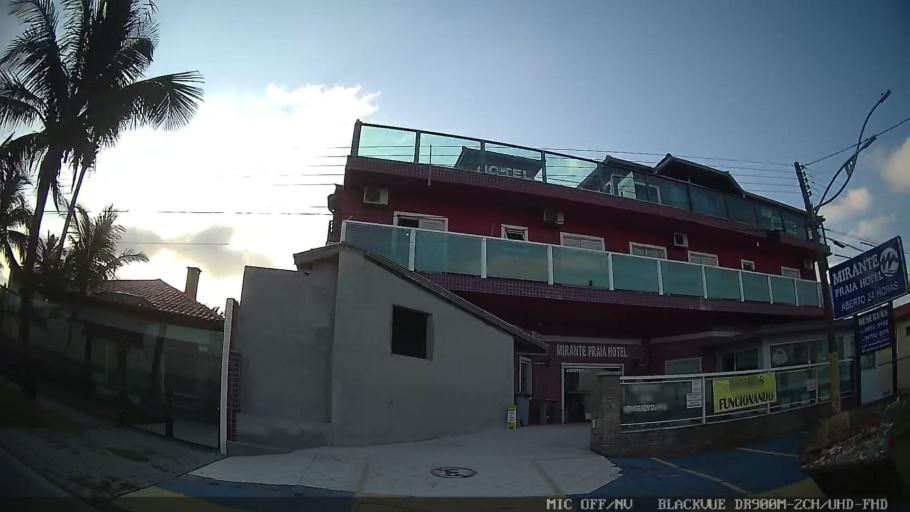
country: BR
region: Sao Paulo
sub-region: Peruibe
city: Peruibe
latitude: -24.3061
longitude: -46.9748
